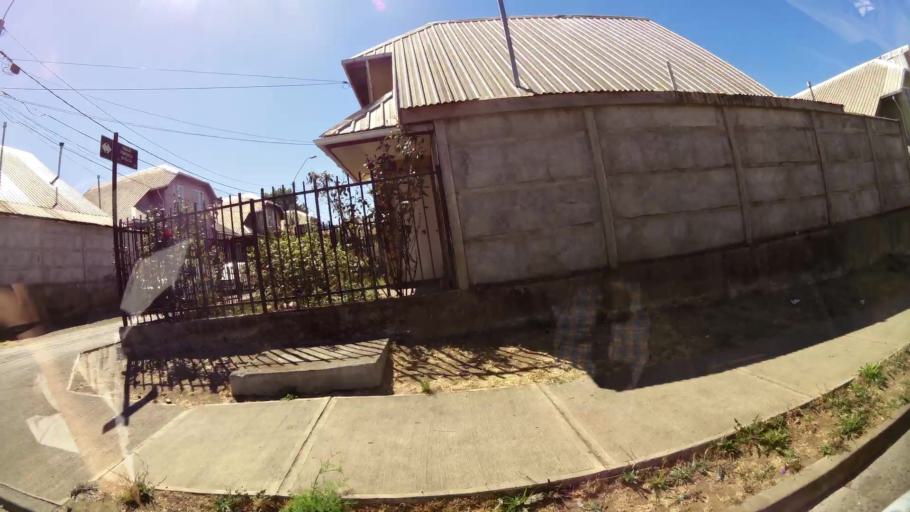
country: CL
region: Biobio
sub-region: Provincia de Concepcion
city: Penco
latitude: -36.7271
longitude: -72.9842
